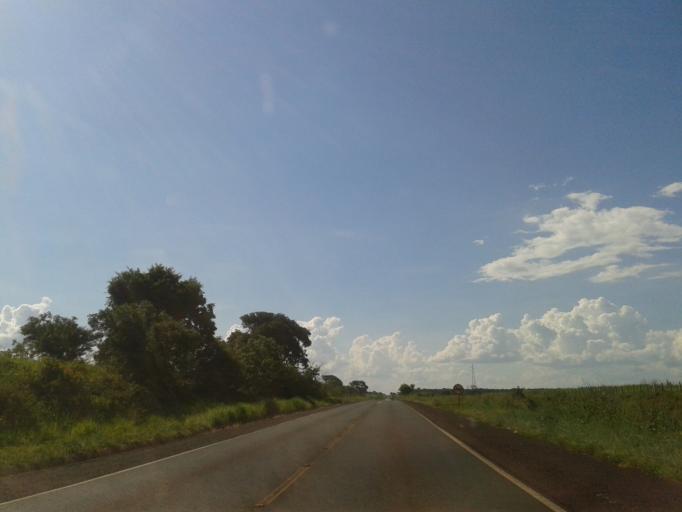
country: BR
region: Minas Gerais
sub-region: Santa Vitoria
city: Santa Vitoria
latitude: -19.0611
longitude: -50.3859
